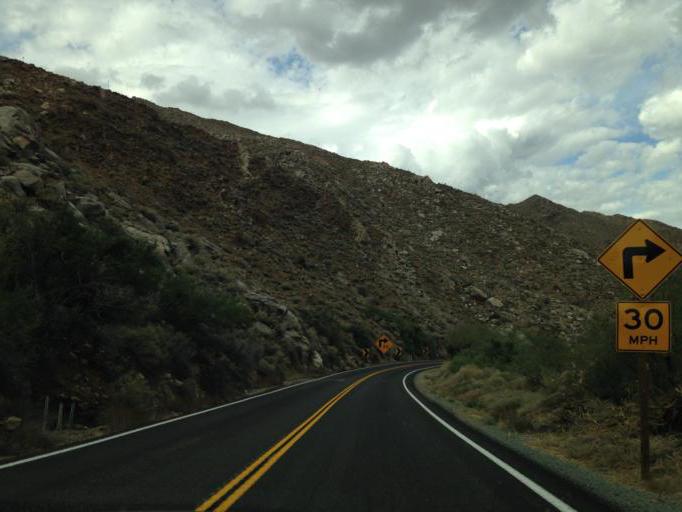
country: US
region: California
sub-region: San Diego County
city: Julian
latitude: 33.1068
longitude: -116.4509
